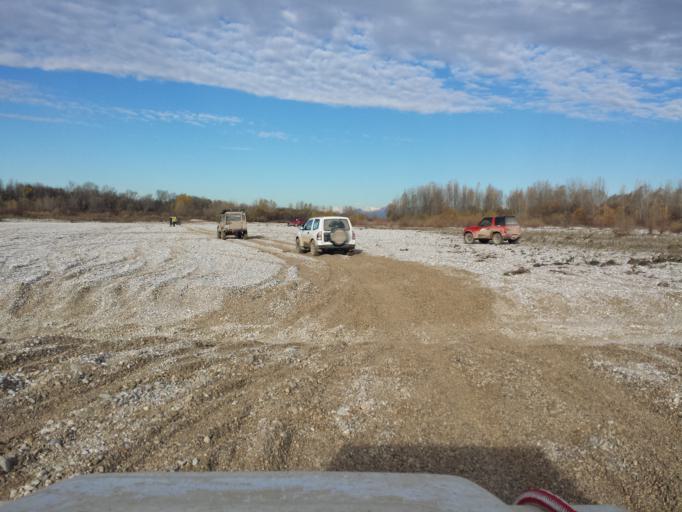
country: IT
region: Friuli Venezia Giulia
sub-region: Provincia di Udine
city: San Vito al Torre
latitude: 45.9072
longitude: 13.3898
